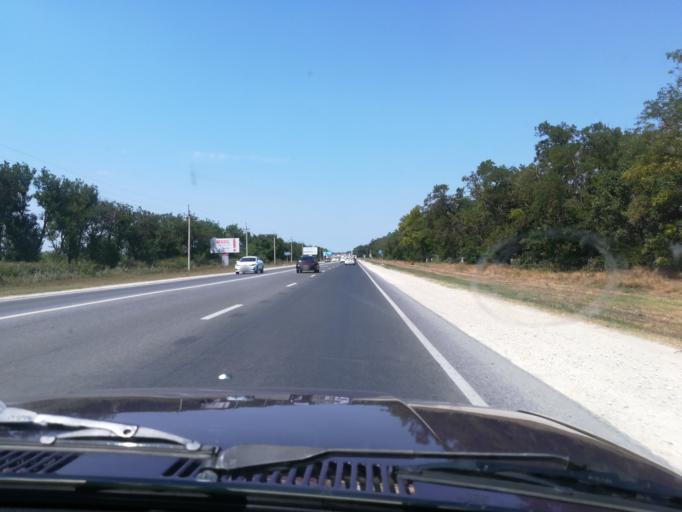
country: RU
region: Krasnodarskiy
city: Tsibanobalka
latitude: 44.9892
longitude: 37.3219
